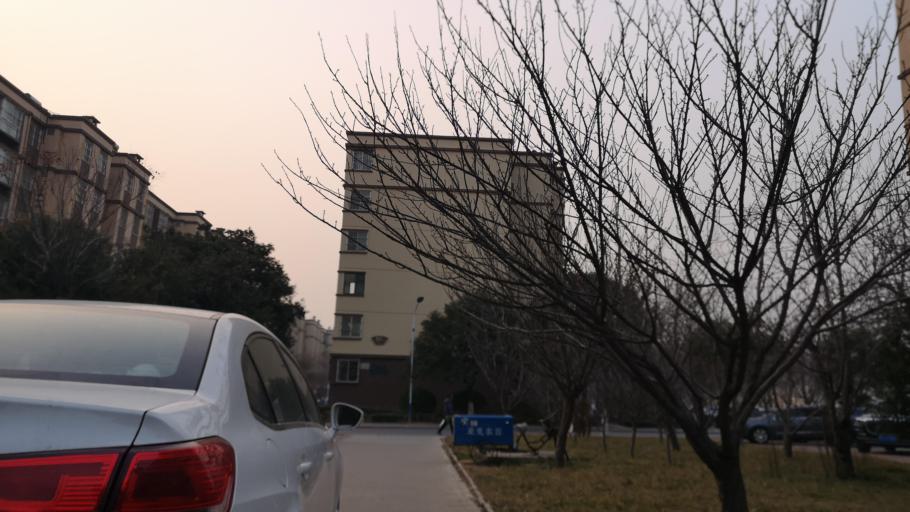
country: CN
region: Henan Sheng
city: Zhongyuanlu
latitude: 35.7859
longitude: 115.0788
